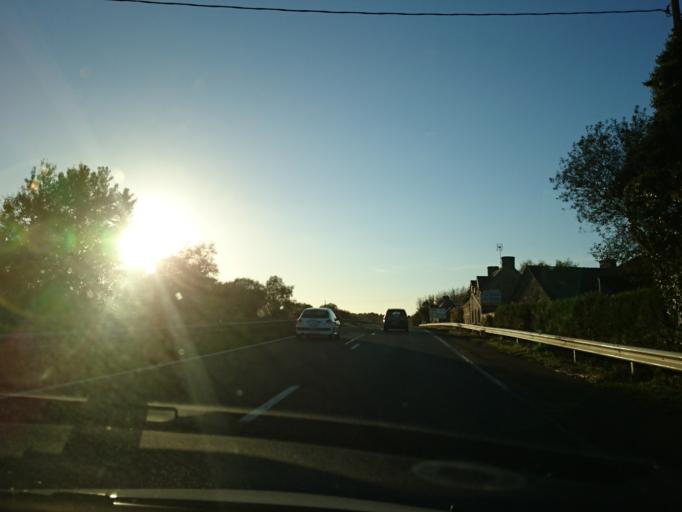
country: FR
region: Brittany
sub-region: Departement des Cotes-d'Armor
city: Louargat
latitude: 48.5676
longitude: -3.3020
